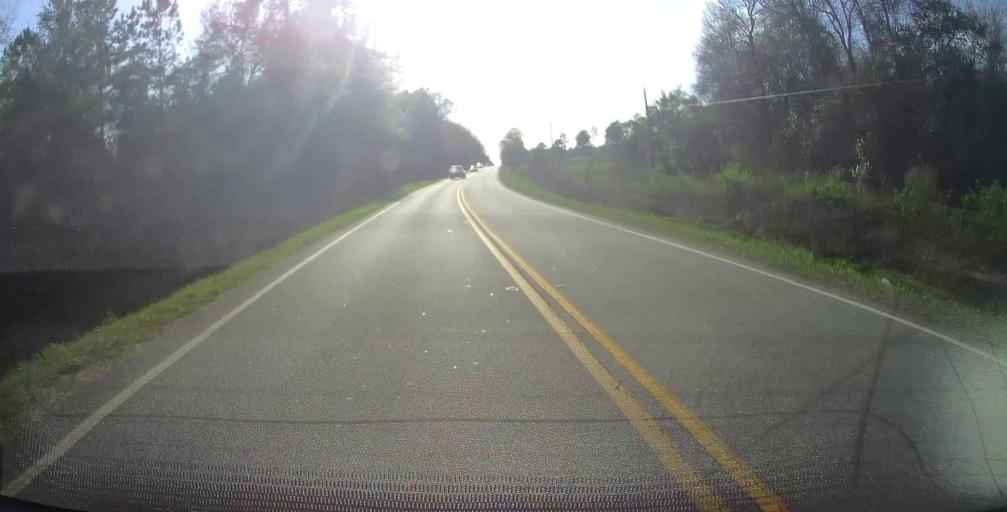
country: US
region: Georgia
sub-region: Montgomery County
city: Mount Vernon
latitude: 32.1865
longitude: -82.6484
